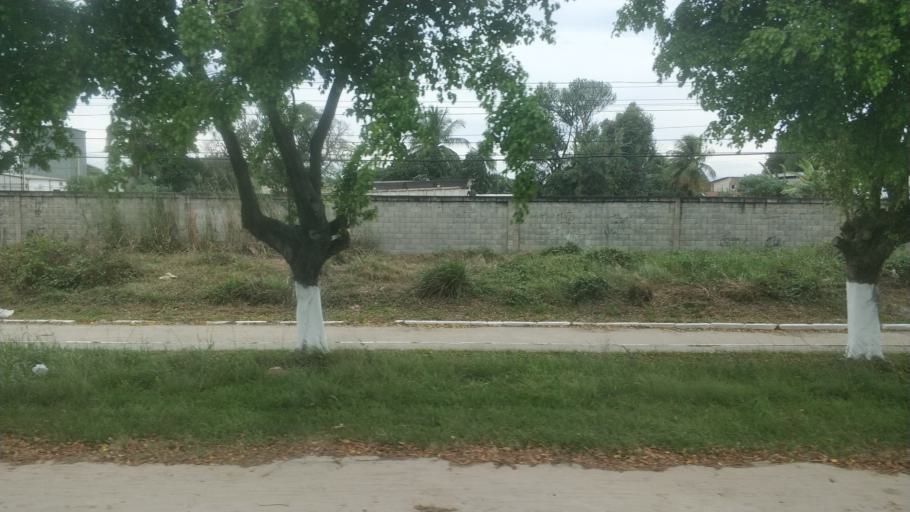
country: BR
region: Rio de Janeiro
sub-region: Seropedica
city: Seropedica
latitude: -22.7978
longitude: -43.6461
